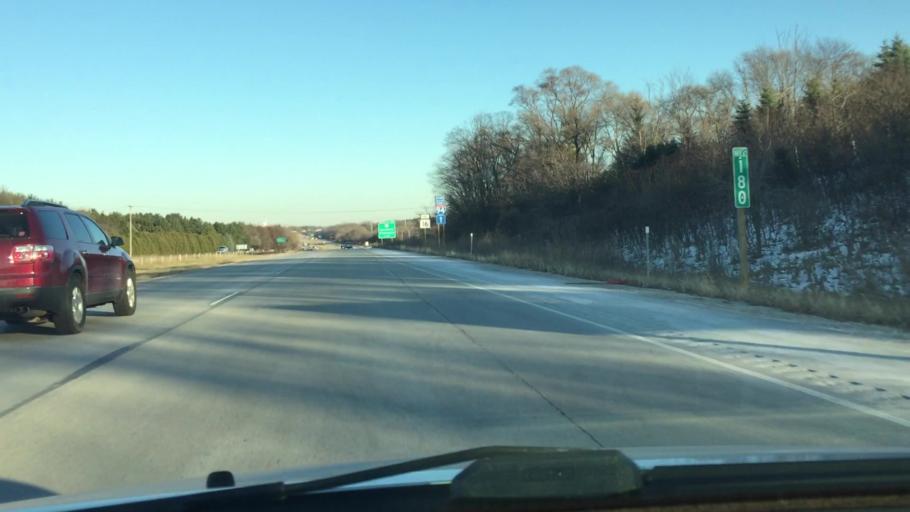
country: US
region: Wisconsin
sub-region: Waukesha County
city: Nashotah
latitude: 43.1018
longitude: -88.3953
